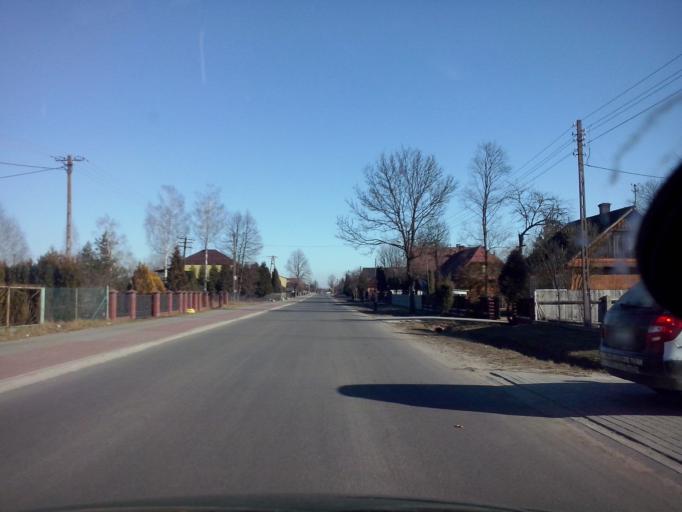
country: PL
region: Subcarpathian Voivodeship
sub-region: Powiat nizanski
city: Harasiuki
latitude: 50.4740
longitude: 22.4795
